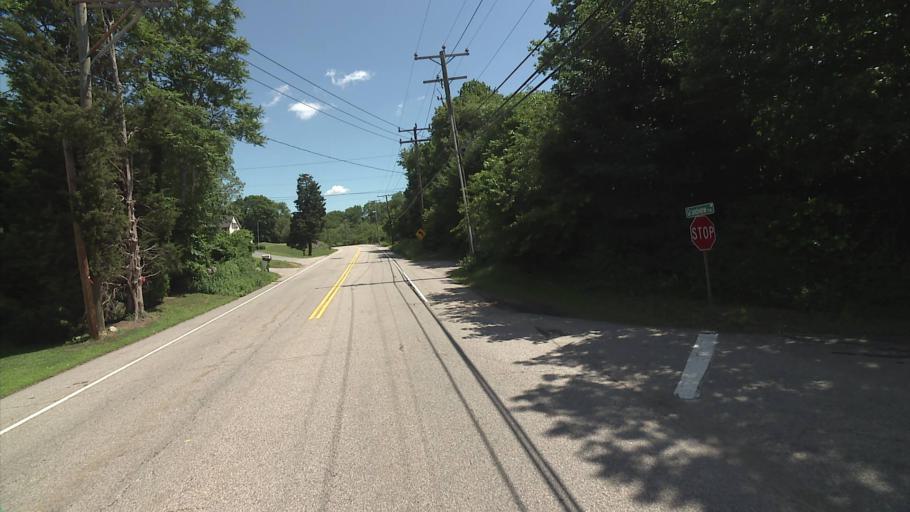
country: US
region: Connecticut
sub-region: New London County
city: Pawcatuck
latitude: 41.3451
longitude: -71.8949
